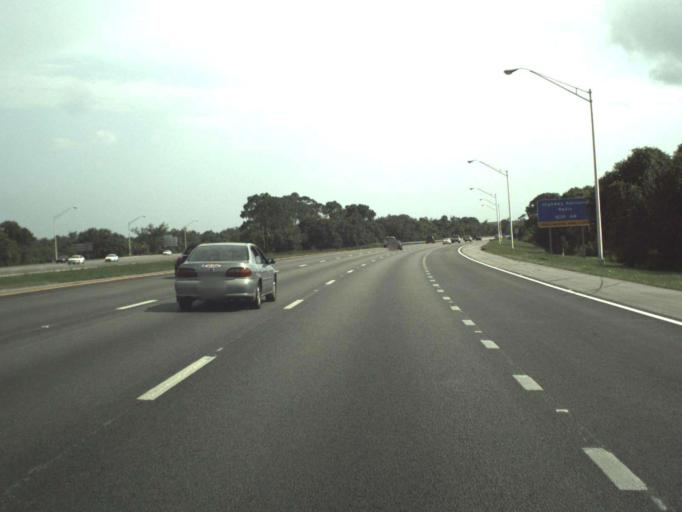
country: US
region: Florida
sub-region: Saint Lucie County
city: Fort Pierce South
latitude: 27.4065
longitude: -80.3887
